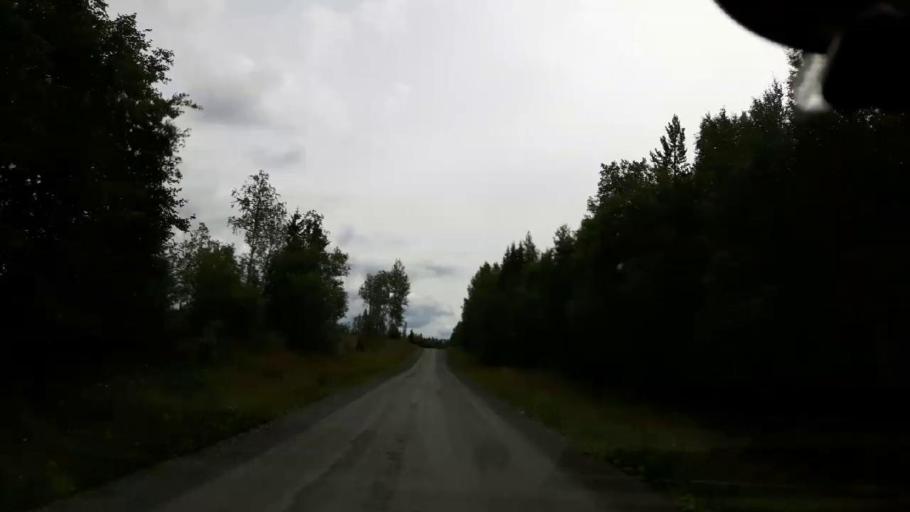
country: SE
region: Jaemtland
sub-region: Krokoms Kommun
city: Valla
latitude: 63.6539
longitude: 13.9805
